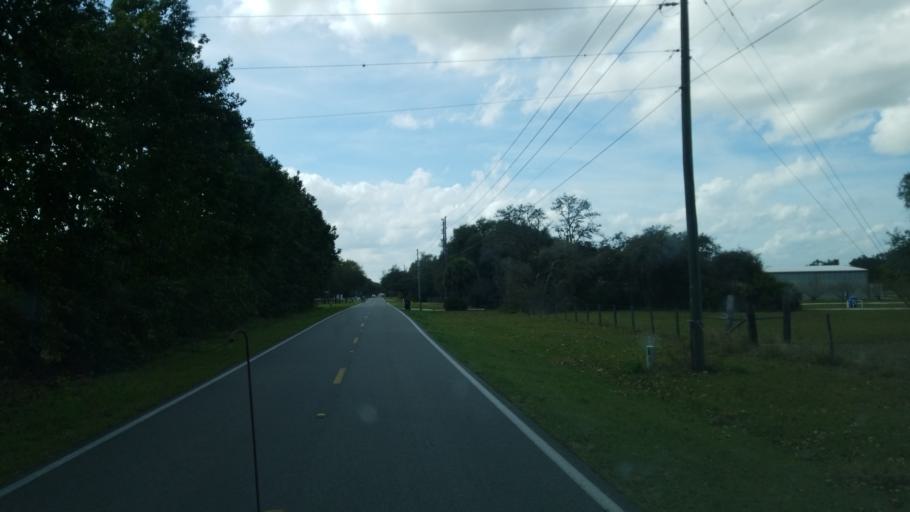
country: US
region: Florida
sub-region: Polk County
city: Lake Wales
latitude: 27.9251
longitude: -81.5198
